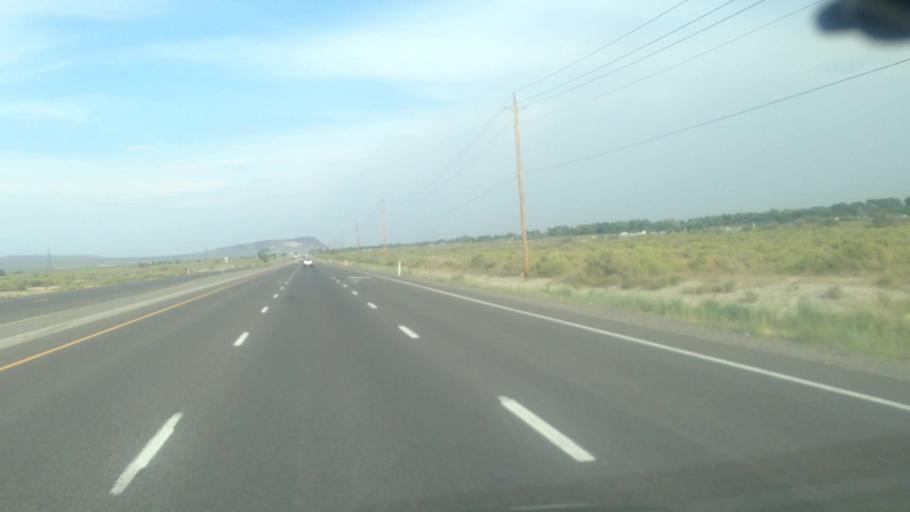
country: US
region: Nevada
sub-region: Lyon County
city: Fernley
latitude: 39.5972
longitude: -119.1895
